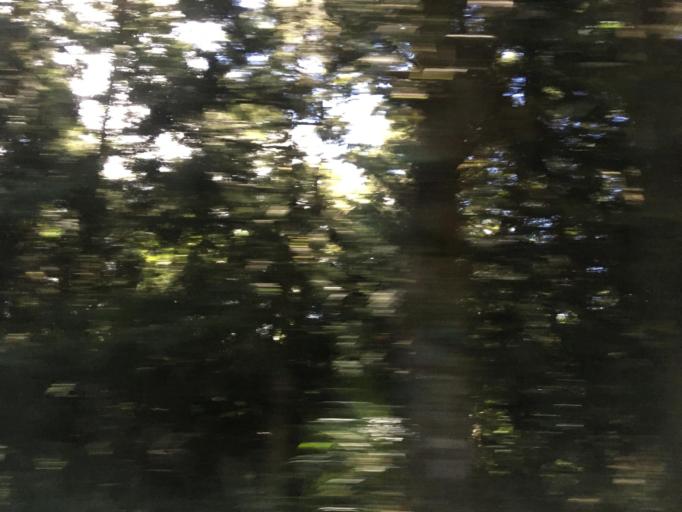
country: TW
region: Taiwan
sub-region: Yilan
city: Yilan
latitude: 24.5112
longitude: 121.5861
